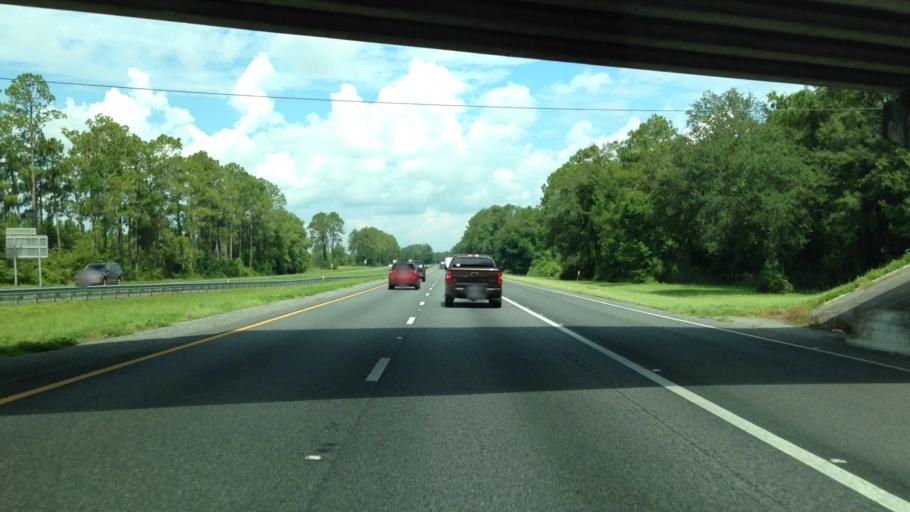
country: US
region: Florida
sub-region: Suwannee County
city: Wellborn
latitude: 30.2806
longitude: -82.8199
